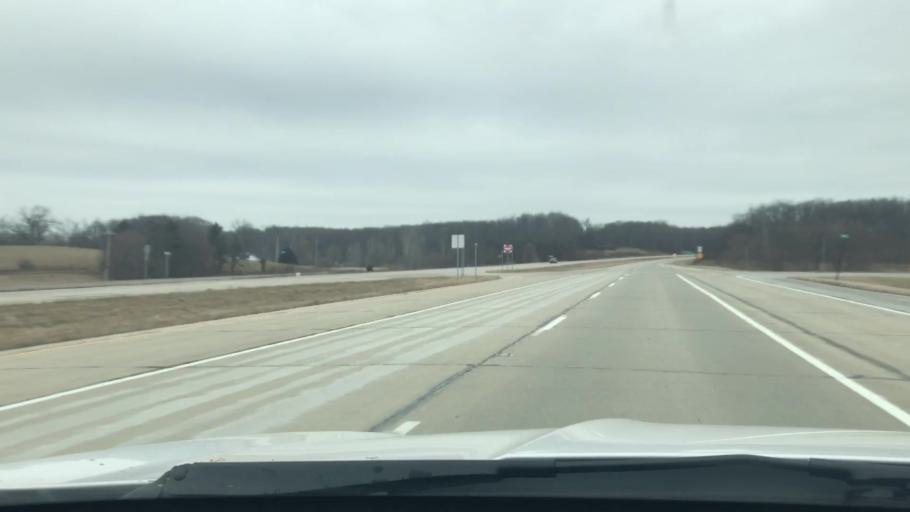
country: US
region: Indiana
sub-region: Miami County
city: Peru
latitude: 40.7645
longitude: -86.1699
